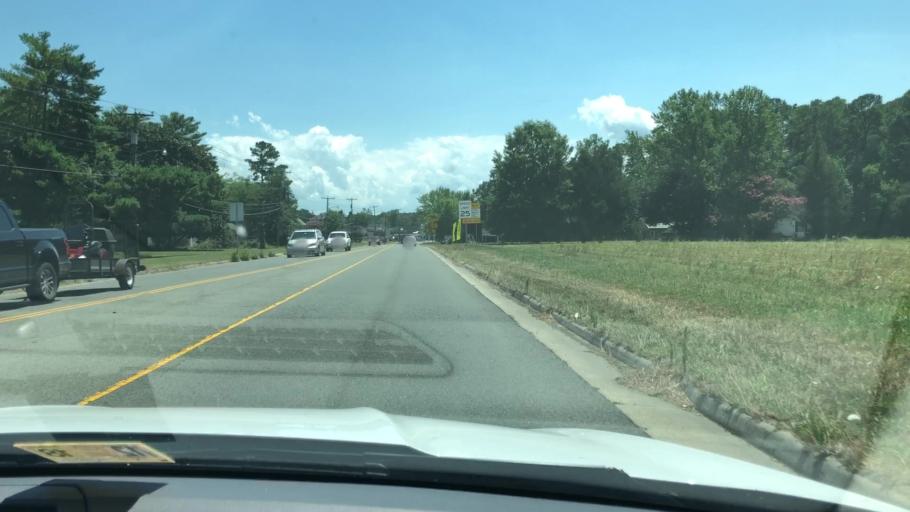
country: US
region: Virginia
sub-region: Lancaster County
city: Kilmarnock
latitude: 37.6524
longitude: -76.3888
